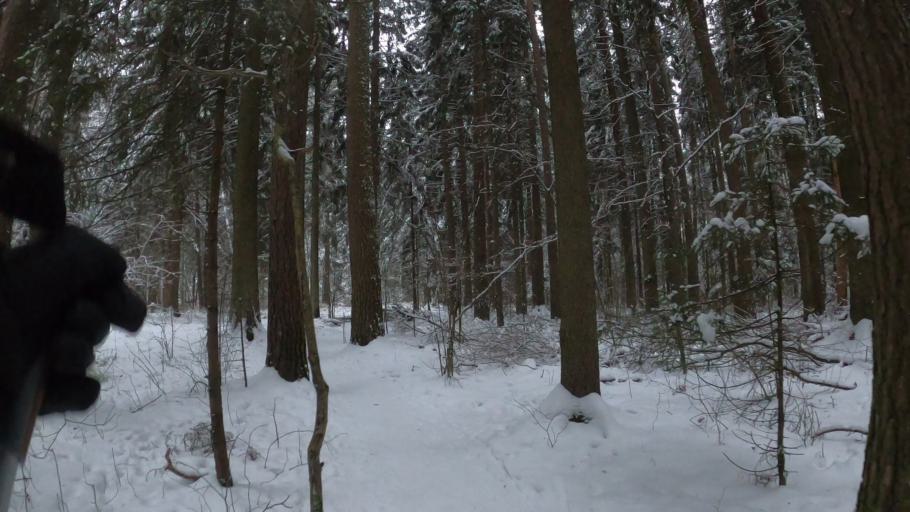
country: RU
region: Moskovskaya
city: Firsanovka
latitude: 55.9274
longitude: 37.2187
